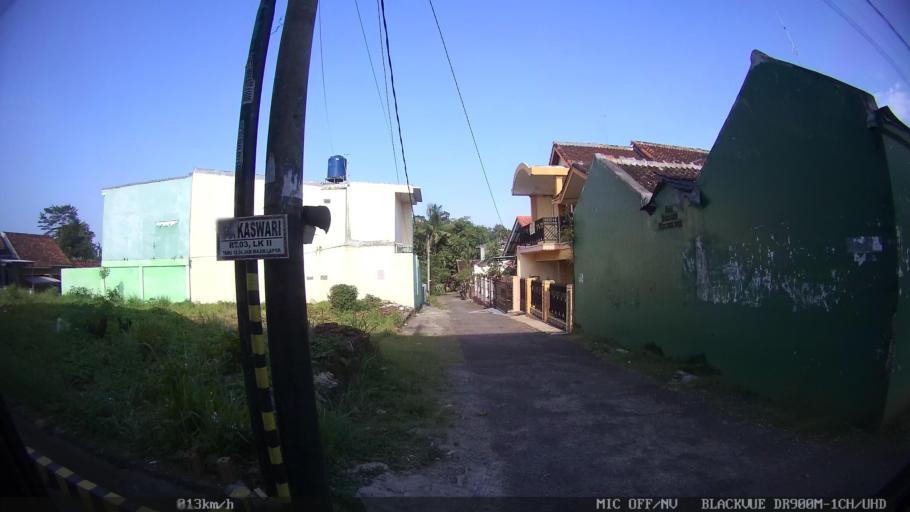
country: ID
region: Lampung
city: Kedaton
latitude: -5.3729
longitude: 105.2348
